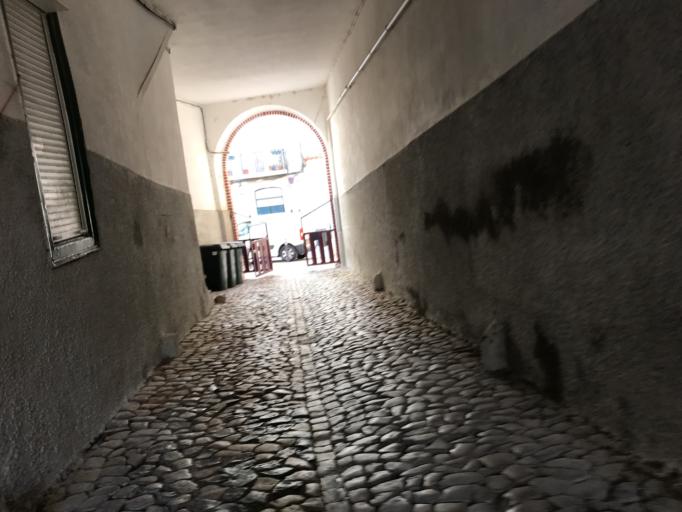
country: PT
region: Lisbon
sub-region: Lisbon
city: Lisbon
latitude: 38.7237
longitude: -9.1414
